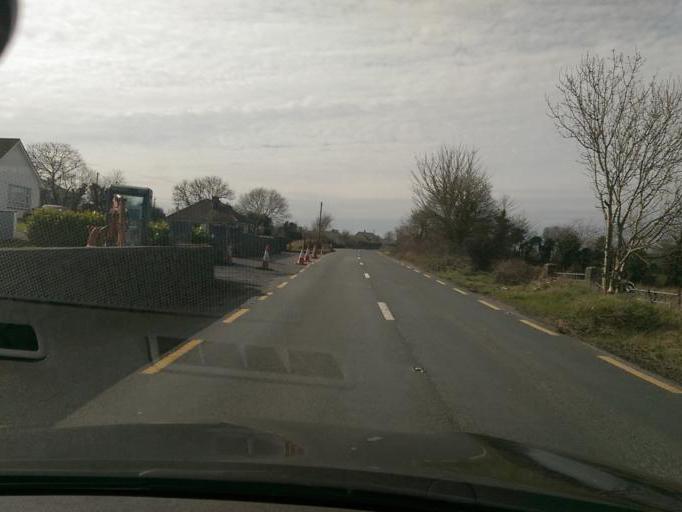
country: IE
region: Connaught
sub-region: County Galway
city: Tuam
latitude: 53.4373
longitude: -8.7408
